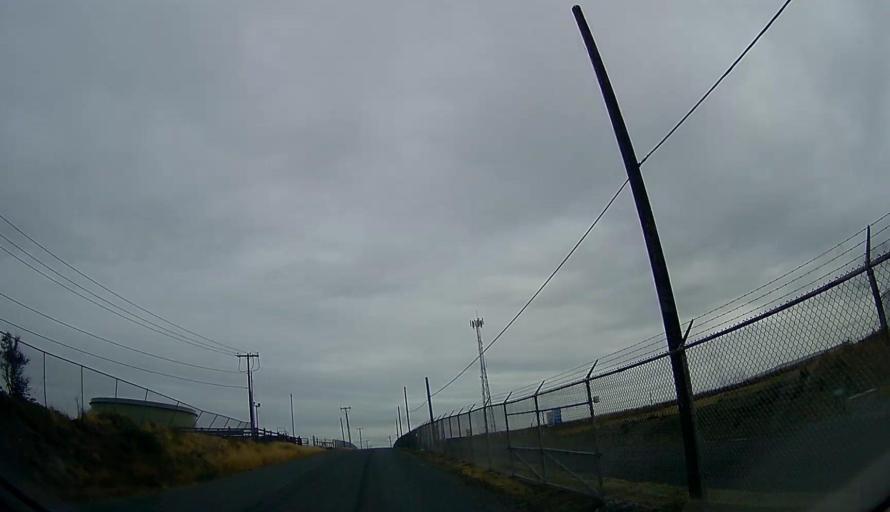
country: US
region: Washington
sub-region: Skagit County
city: Anacortes
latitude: 48.4784
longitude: -122.5655
